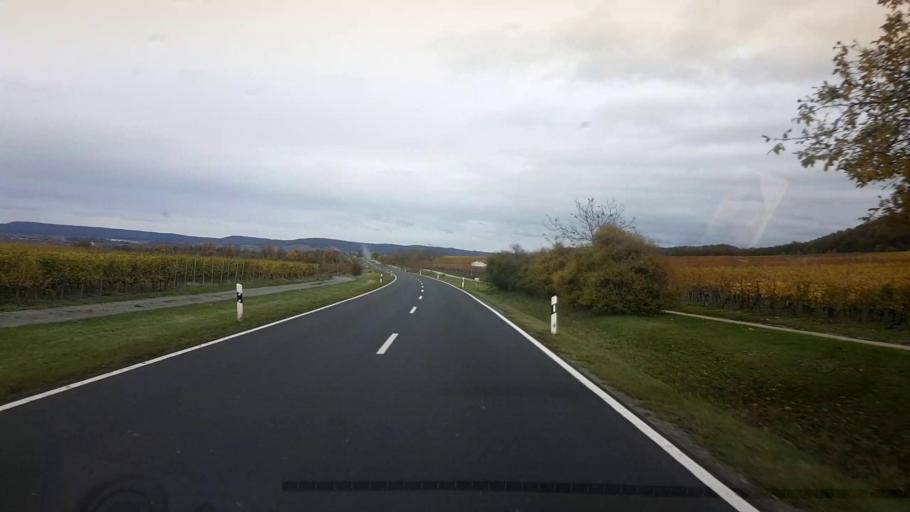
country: DE
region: Bavaria
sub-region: Regierungsbezirk Unterfranken
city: Rodelsee
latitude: 49.7354
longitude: 10.2755
